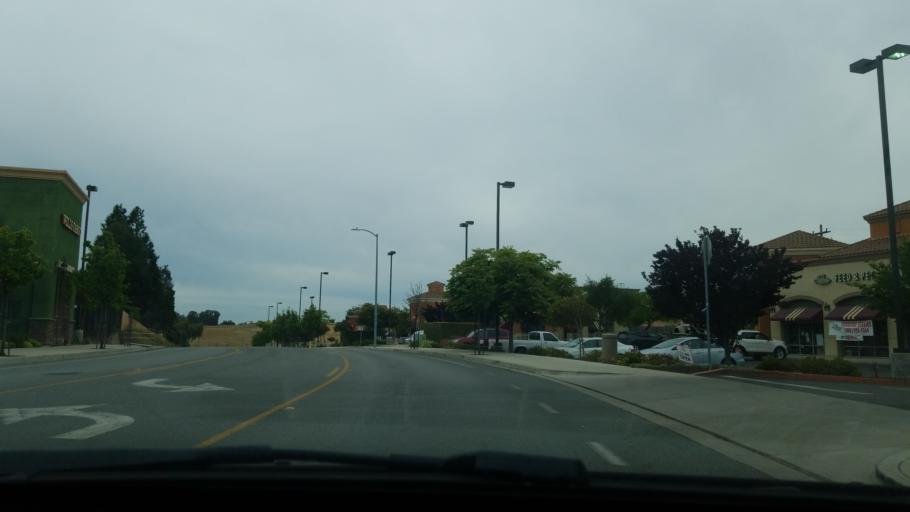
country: US
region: California
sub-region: San Luis Obispo County
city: Nipomo
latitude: 35.0352
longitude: -120.4863
